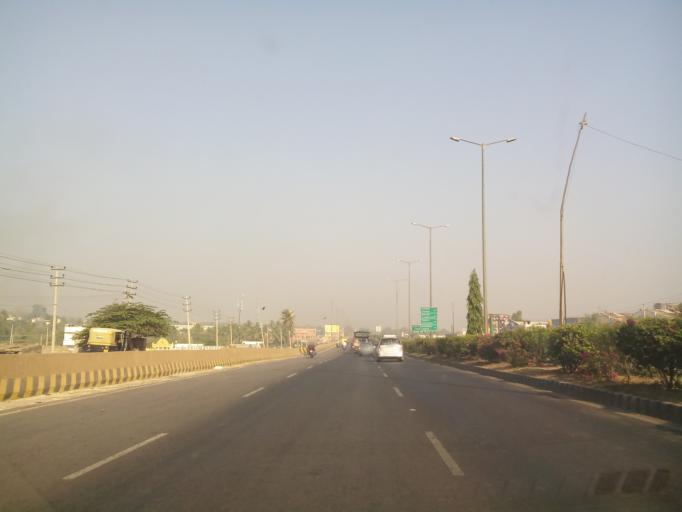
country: IN
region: Karnataka
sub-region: Bangalore Rural
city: Nelamangala
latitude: 13.0669
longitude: 77.4512
